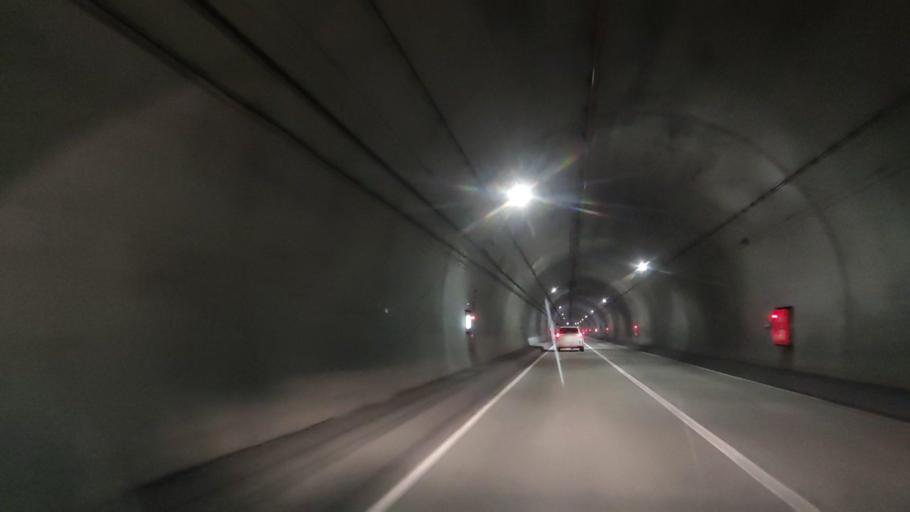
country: JP
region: Hokkaido
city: Rumoi
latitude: 43.7149
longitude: 141.3301
